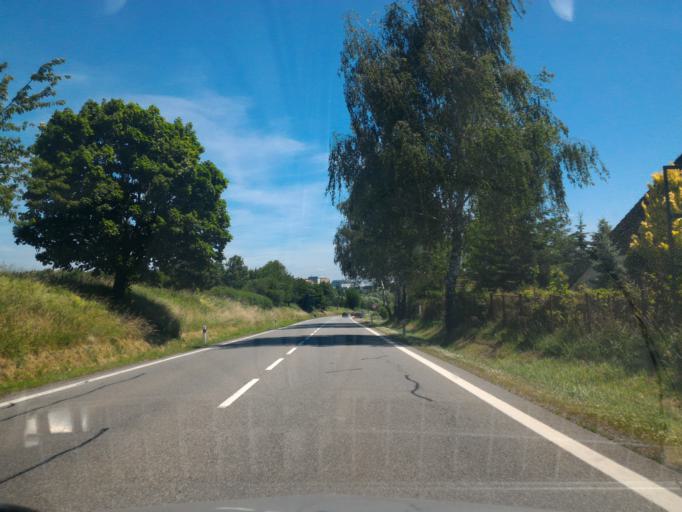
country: CZ
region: Vysocina
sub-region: Okres Jihlava
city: Jihlava
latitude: 49.3934
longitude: 15.5552
